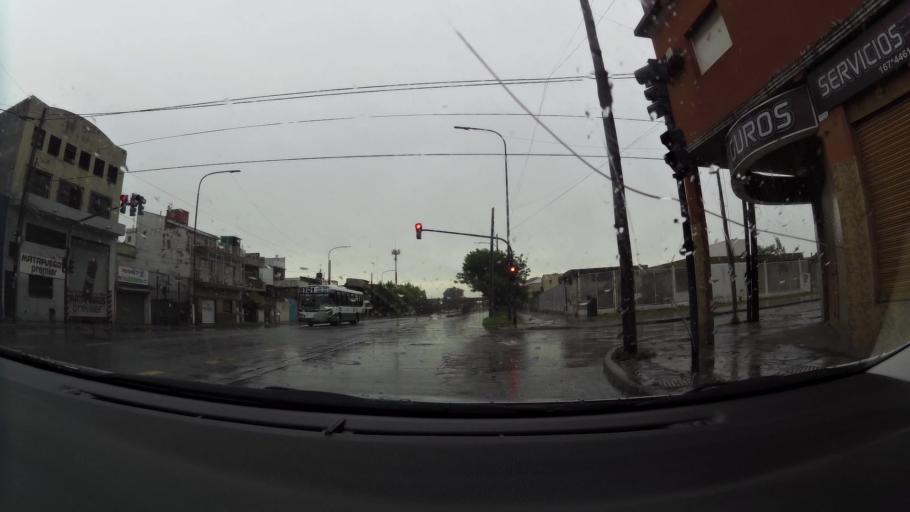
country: AR
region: Buenos Aires F.D.
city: Villa Lugano
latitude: -34.6632
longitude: -58.4475
